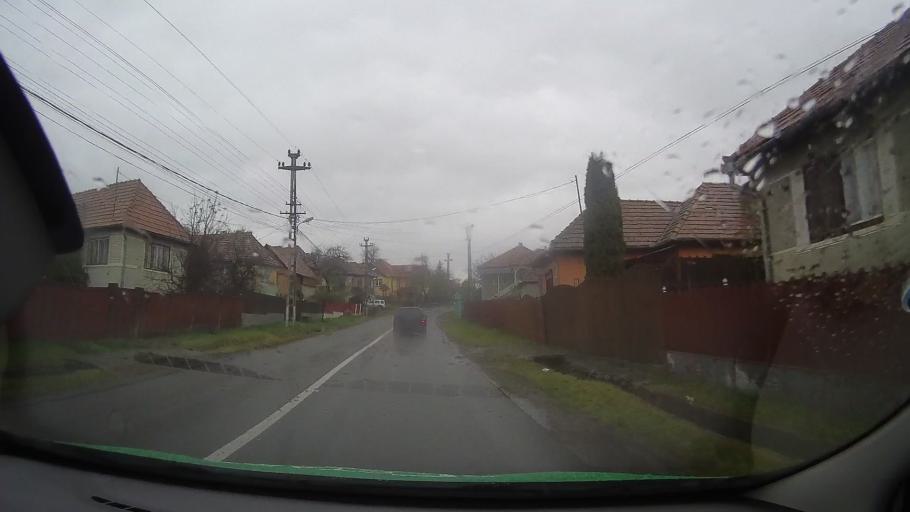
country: RO
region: Mures
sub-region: Comuna Brancovenesti
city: Valenii de Mures
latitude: 46.8946
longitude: 24.7964
